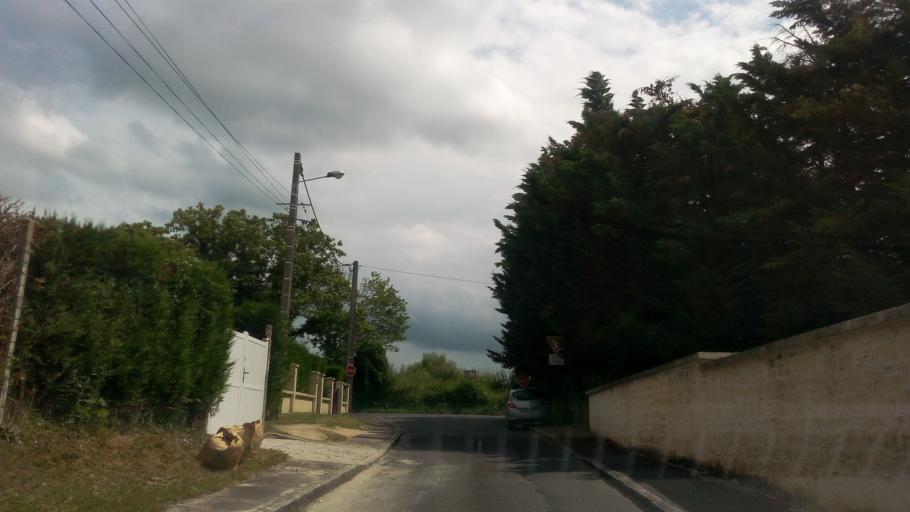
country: FR
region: Picardie
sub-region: Departement de l'Oise
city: Saint-Maximin
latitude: 49.2209
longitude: 2.4460
